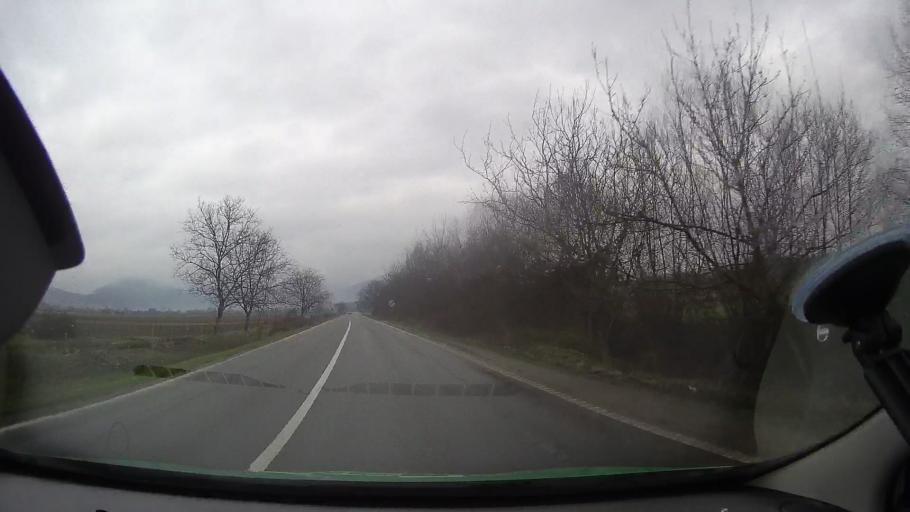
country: RO
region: Arad
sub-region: Comuna Gurahont
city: Gurahont
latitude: 46.2718
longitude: 22.3111
